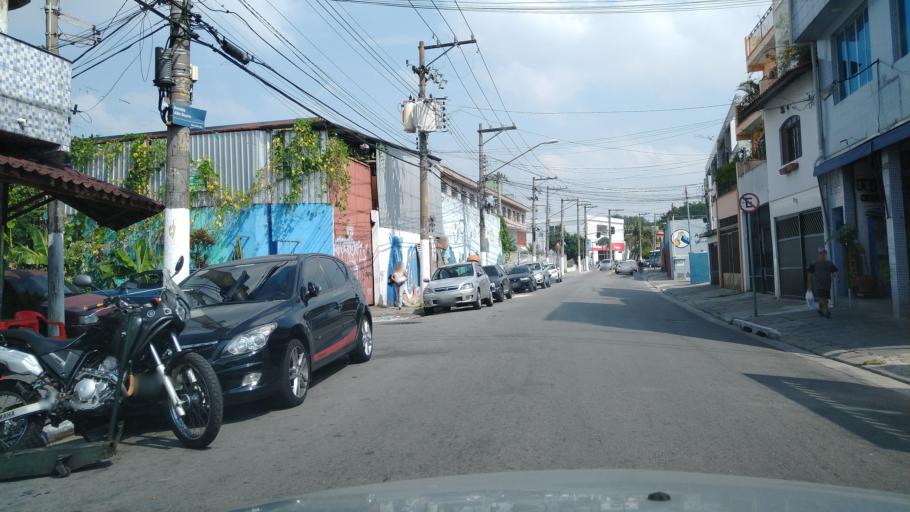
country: BR
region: Sao Paulo
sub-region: Guarulhos
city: Guarulhos
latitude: -23.4778
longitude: -46.5823
